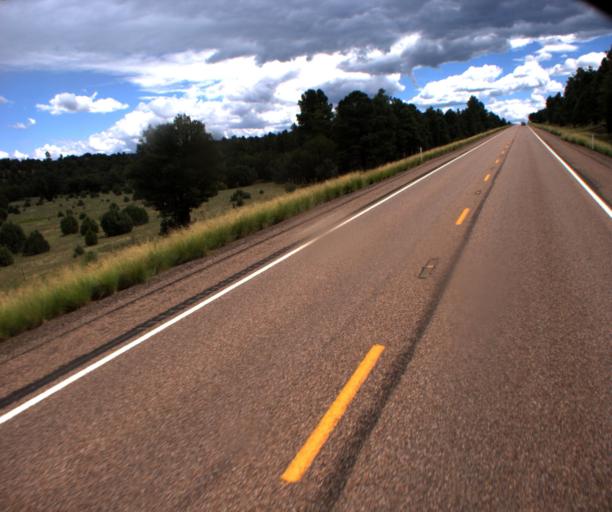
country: US
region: Arizona
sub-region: Navajo County
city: Linden
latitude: 34.3050
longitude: -110.2055
